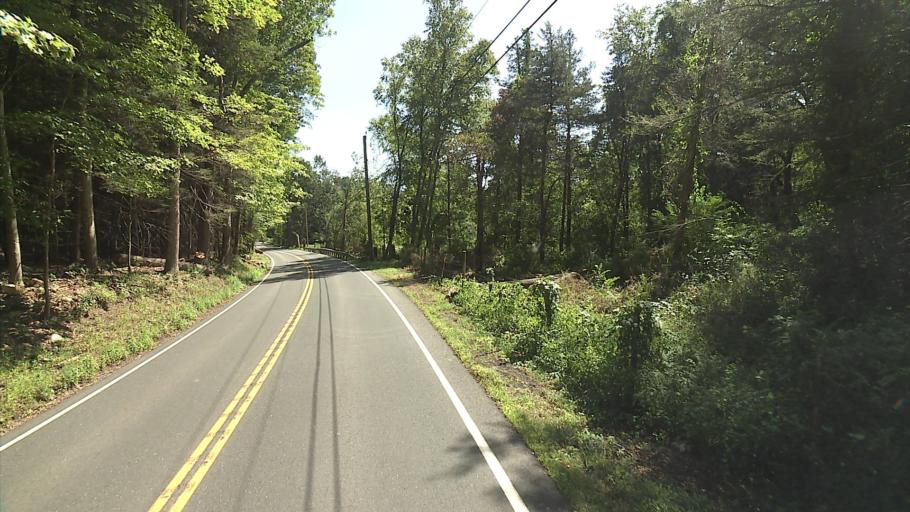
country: US
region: Connecticut
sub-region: New Haven County
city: Oxford
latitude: 41.4491
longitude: -73.1621
